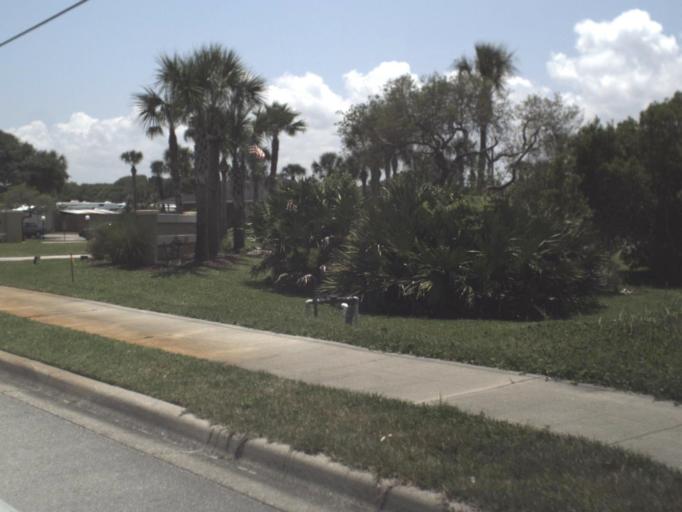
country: US
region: Florida
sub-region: Saint Johns County
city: Butler Beach
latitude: 29.8069
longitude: -81.2662
